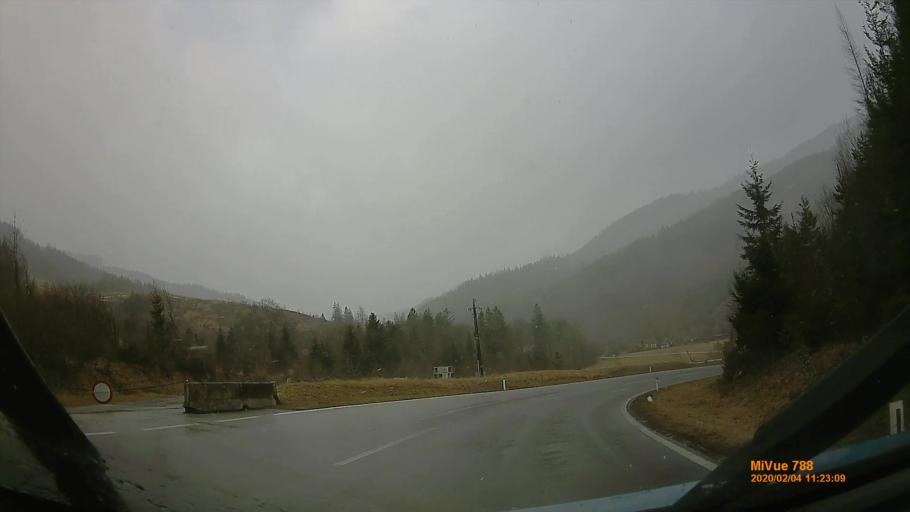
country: AT
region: Styria
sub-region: Politischer Bezirk Bruck-Muerzzuschlag
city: Muerzzuschlag
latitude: 47.6167
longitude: 15.6666
